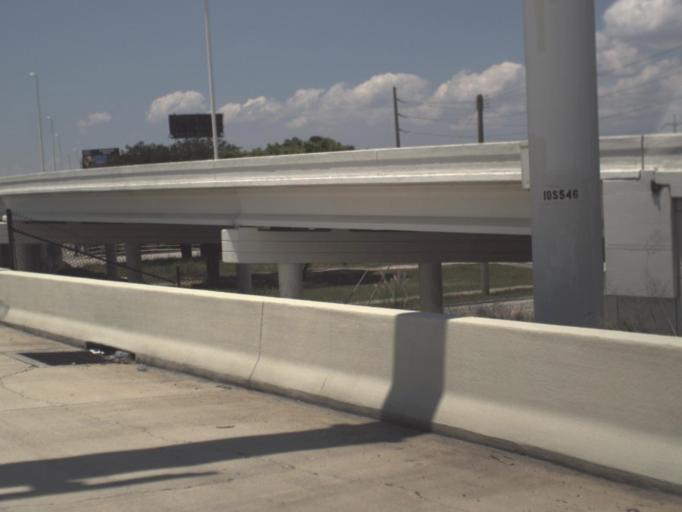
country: US
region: Florida
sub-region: Hillsborough County
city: Tampa
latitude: 27.9570
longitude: -82.4576
